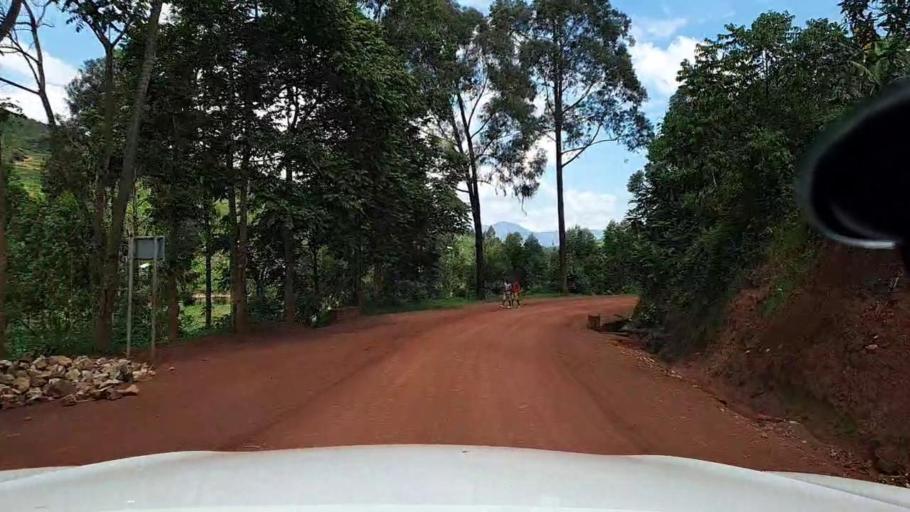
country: RW
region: Northern Province
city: Byumba
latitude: -1.7347
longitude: 29.8567
